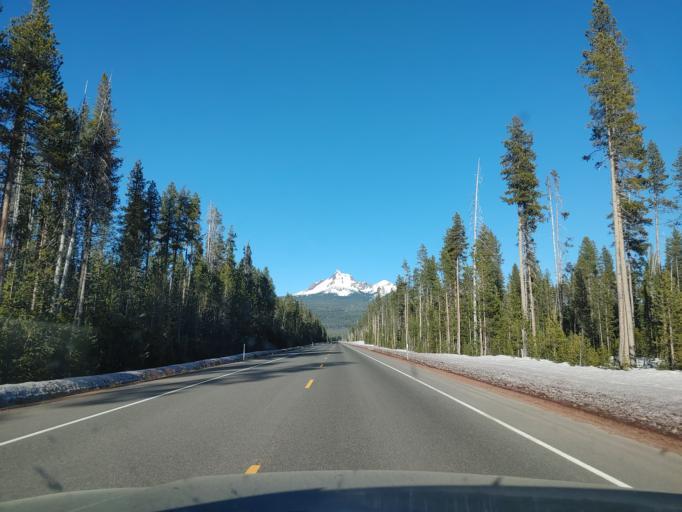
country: US
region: Oregon
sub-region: Lane County
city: Oakridge
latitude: 43.1185
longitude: -122.1609
